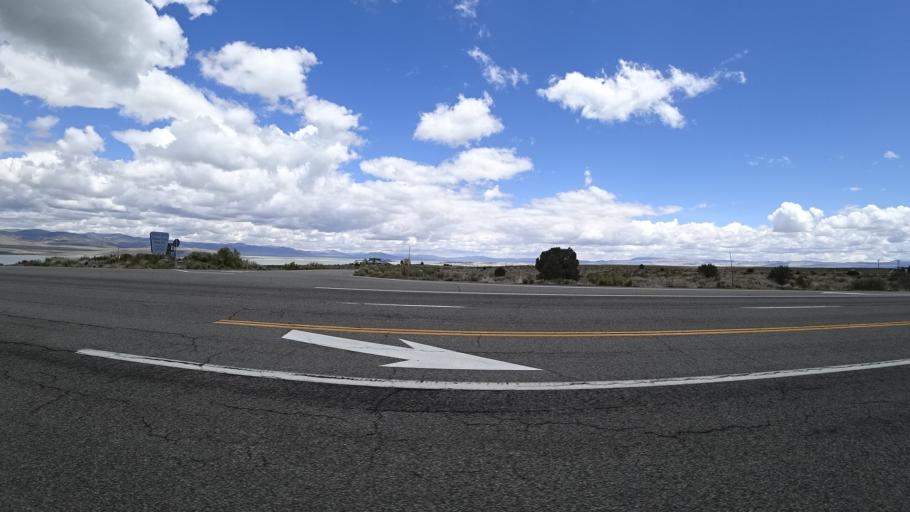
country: US
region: California
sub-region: Mono County
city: Bridgeport
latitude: 37.9636
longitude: -119.1245
